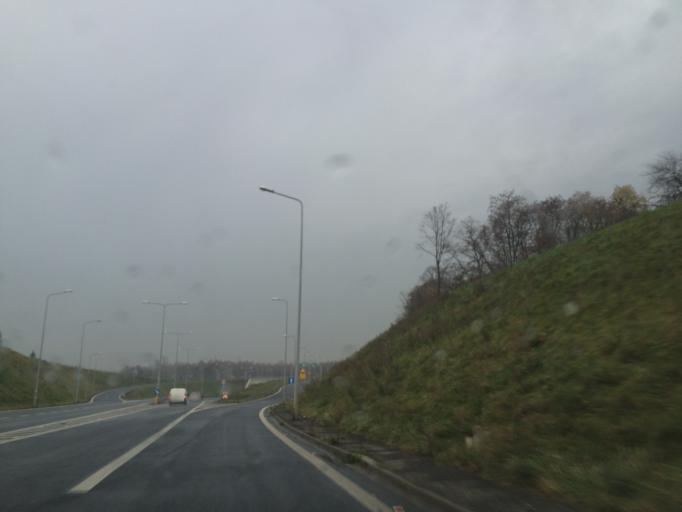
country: PL
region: Silesian Voivodeship
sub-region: Powiat tarnogorski
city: Radzionkow
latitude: 50.3571
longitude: 18.8679
